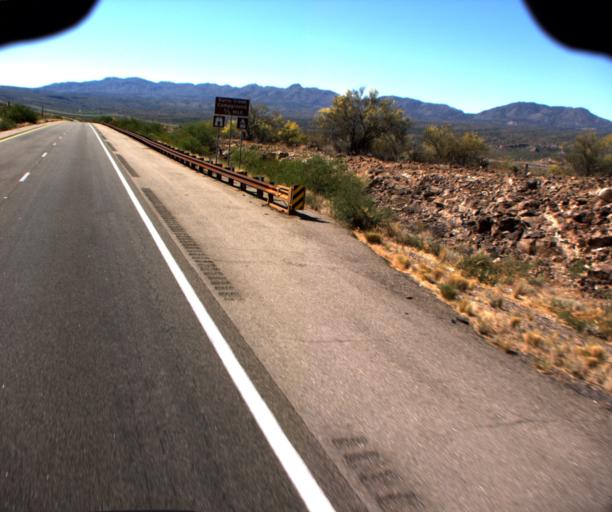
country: US
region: Arizona
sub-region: Yavapai County
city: Bagdad
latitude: 34.5406
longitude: -113.4365
